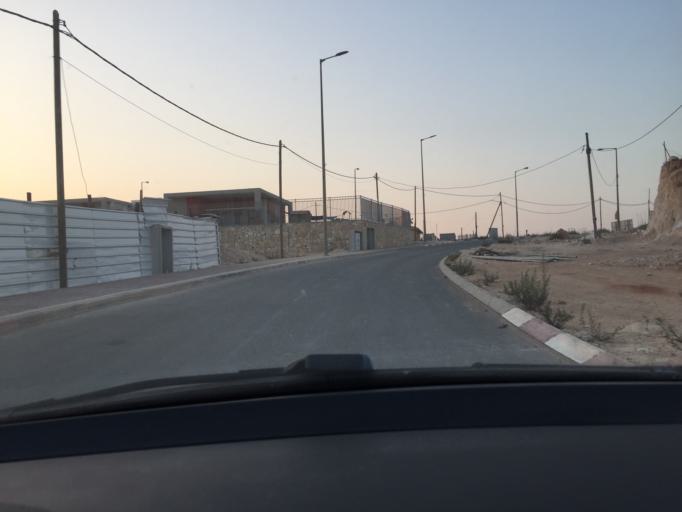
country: PS
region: West Bank
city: Bruqin
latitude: 32.0800
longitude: 35.0880
